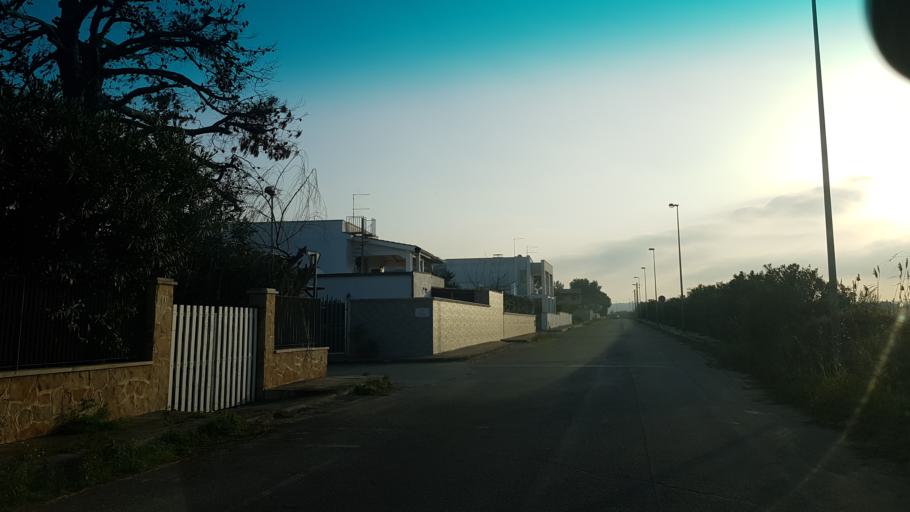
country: IT
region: Apulia
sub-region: Provincia di Brindisi
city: Carovigno
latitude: 40.7492
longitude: 17.7191
